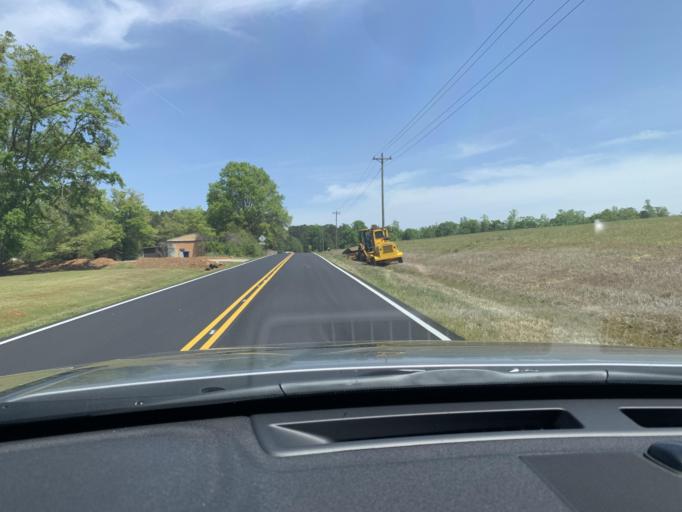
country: US
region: Georgia
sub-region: Oconee County
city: Bogart
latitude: 33.8966
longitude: -83.5017
